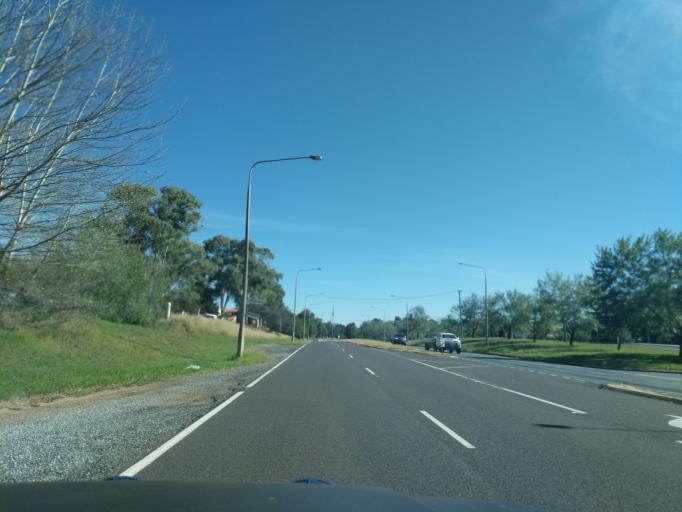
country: AU
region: Australian Capital Territory
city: Forrest
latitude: -35.3408
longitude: 149.1521
